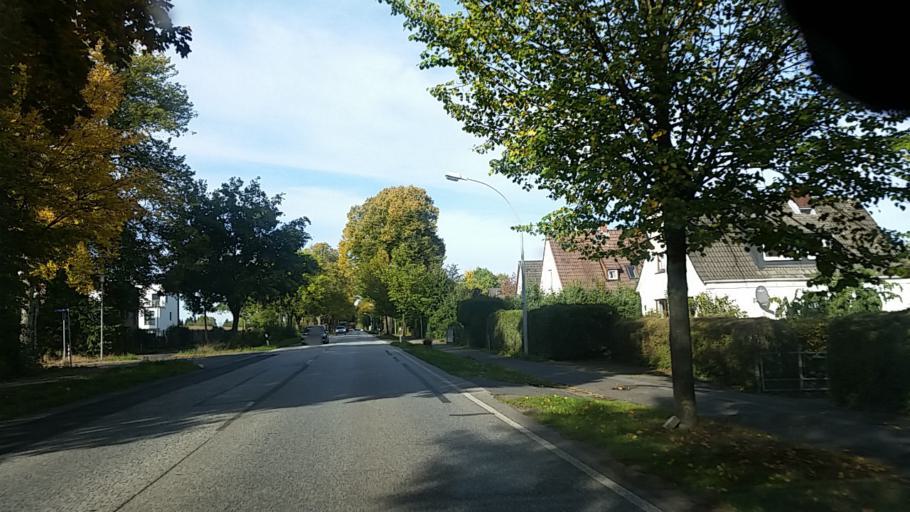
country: DE
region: Schleswig-Holstein
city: Delingsdorf
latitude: 53.6890
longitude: 10.2413
